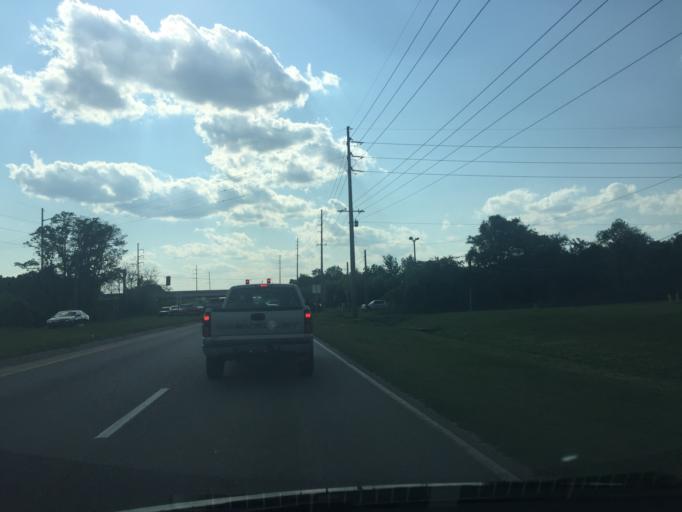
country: US
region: Georgia
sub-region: Chatham County
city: Savannah
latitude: 32.0728
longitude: -81.0702
